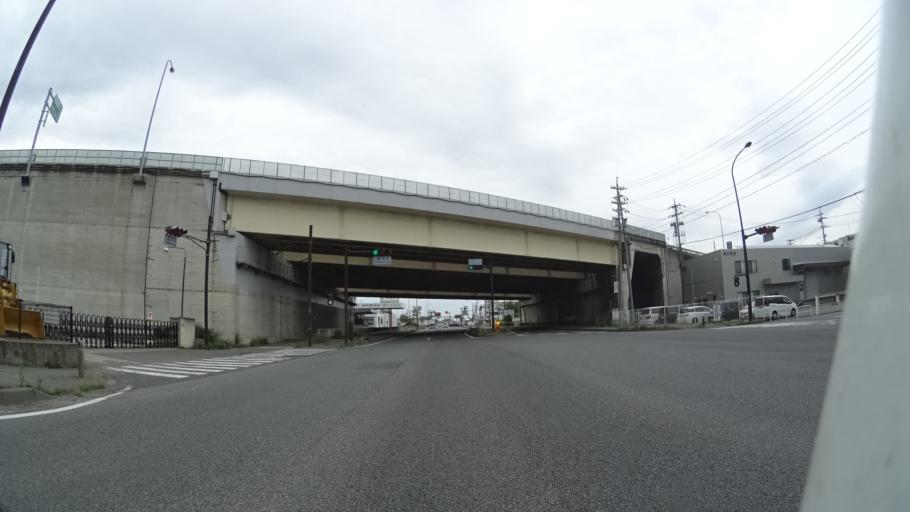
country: JP
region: Nagano
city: Nagano-shi
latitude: 36.5515
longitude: 138.1355
